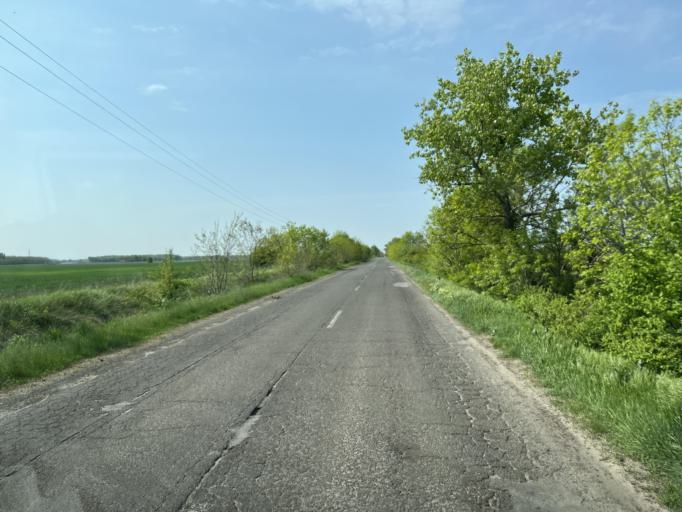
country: HU
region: Pest
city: Nagykoros
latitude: 47.0413
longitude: 19.8300
